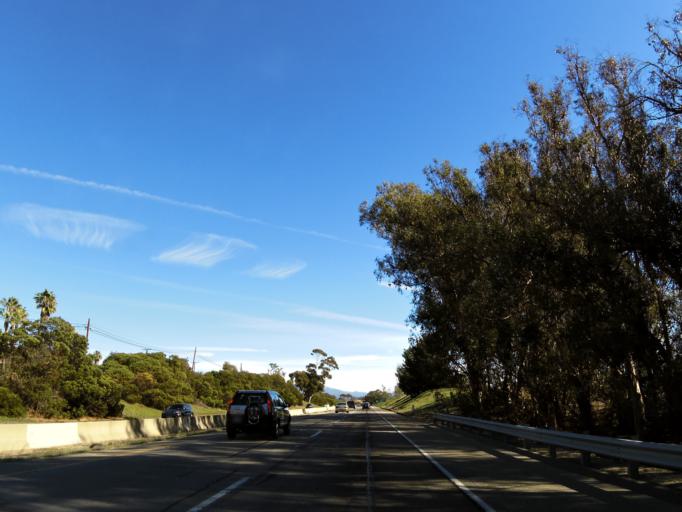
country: US
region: California
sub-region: Santa Barbara County
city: Isla Vista
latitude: 34.4323
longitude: -119.8904
